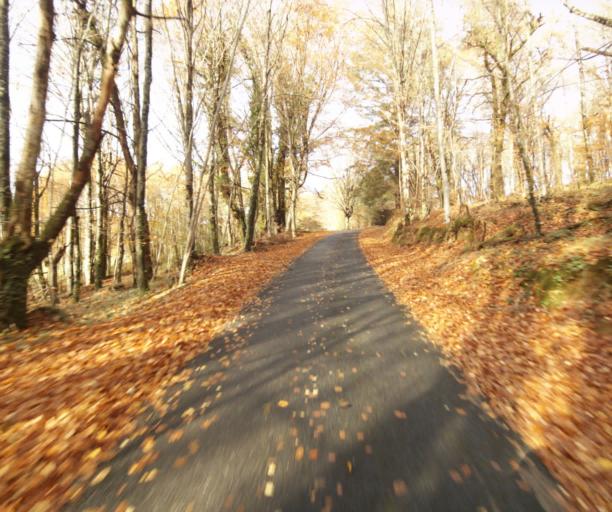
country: FR
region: Limousin
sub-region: Departement de la Correze
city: Cornil
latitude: 45.1988
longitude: 1.7025
